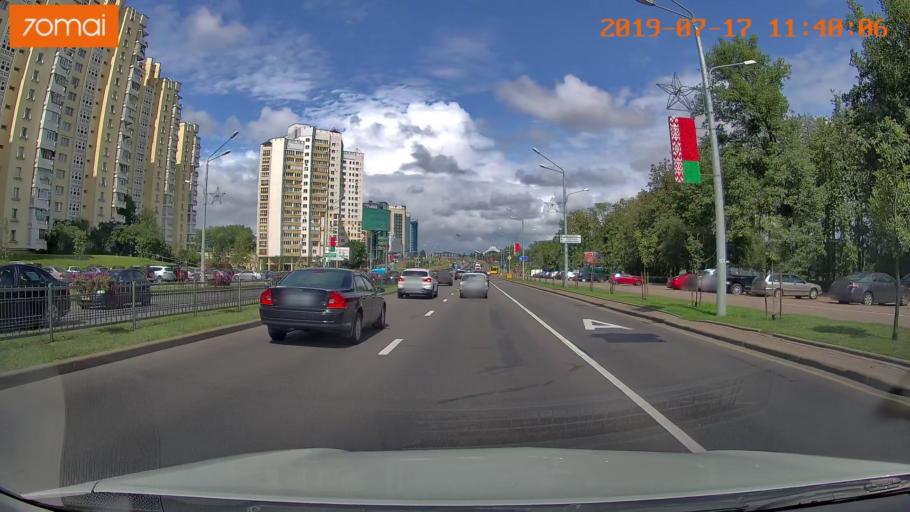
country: BY
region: Minsk
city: Minsk
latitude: 53.9191
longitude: 27.5317
